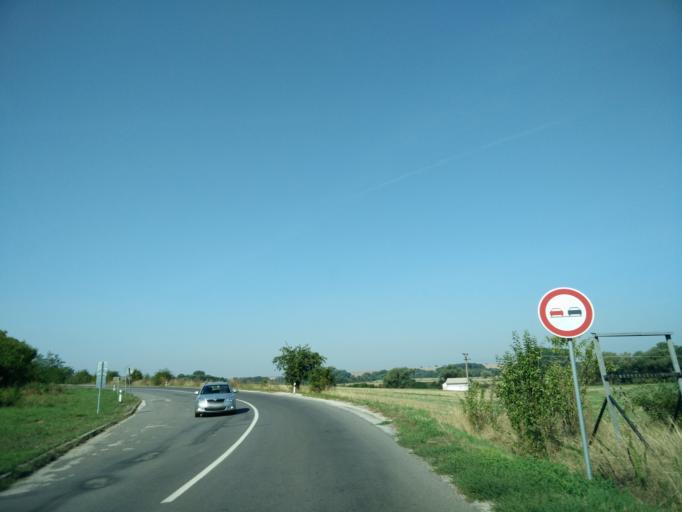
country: SK
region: Nitriansky
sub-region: Okres Nitra
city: Nitra
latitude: 48.3905
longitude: 18.1021
